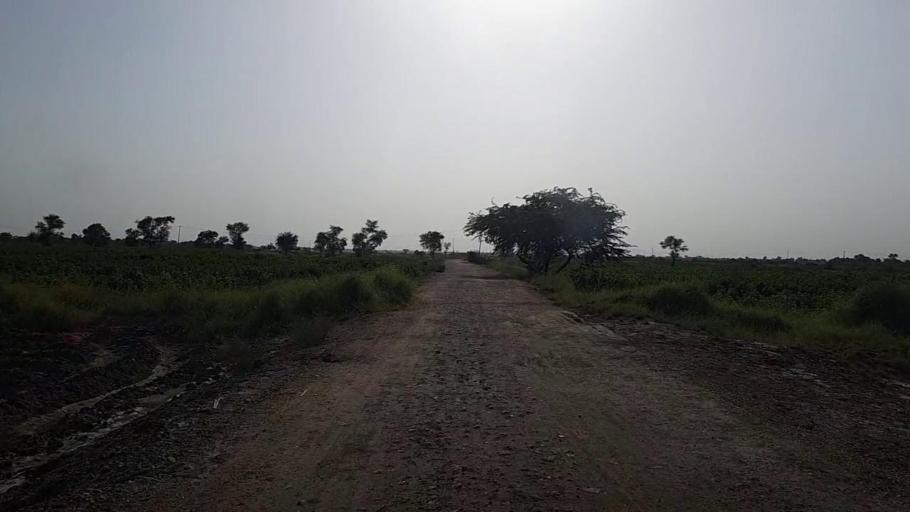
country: PK
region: Sindh
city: Pad Idan
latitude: 26.8531
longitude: 68.3057
